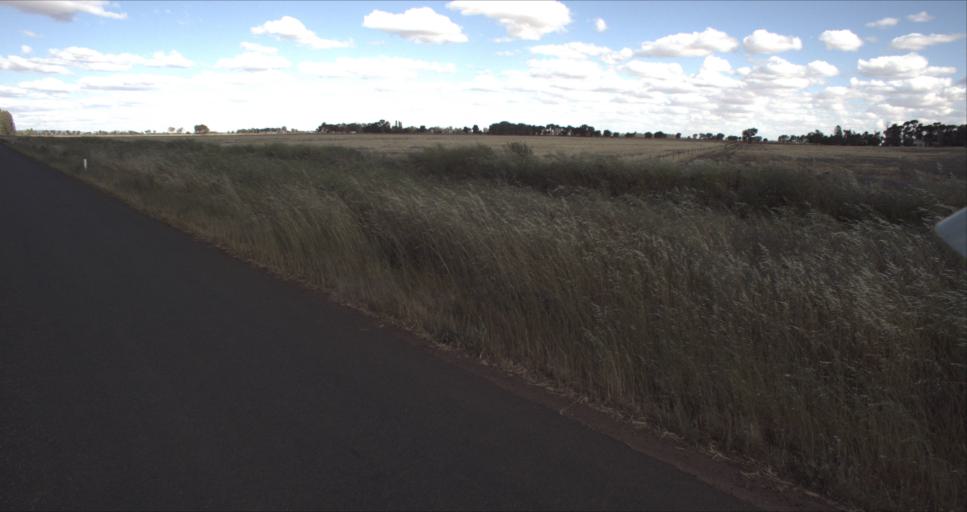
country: AU
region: New South Wales
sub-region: Griffith
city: Griffith
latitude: -34.4373
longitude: 146.2001
